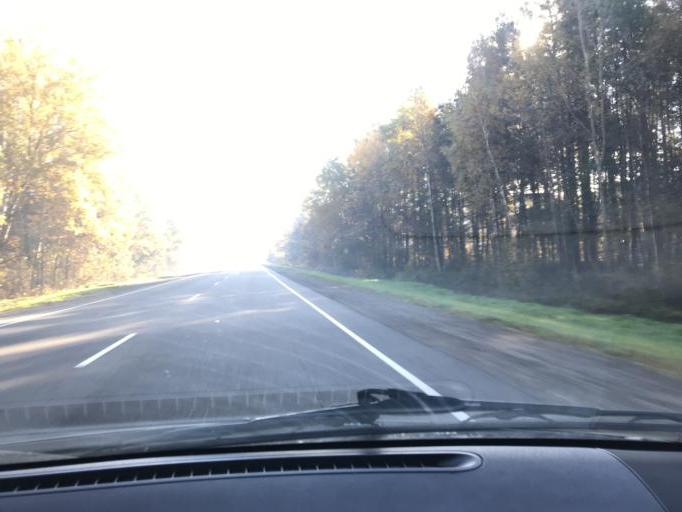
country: BY
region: Brest
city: Horad Luninyets
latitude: 52.2830
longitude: 26.8137
